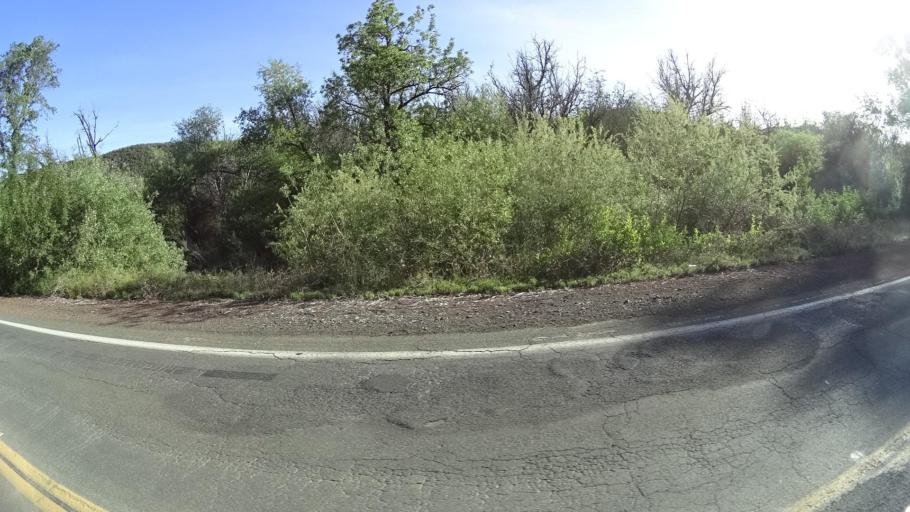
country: US
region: California
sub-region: Lake County
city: North Lakeport
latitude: 39.0924
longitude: -122.9525
